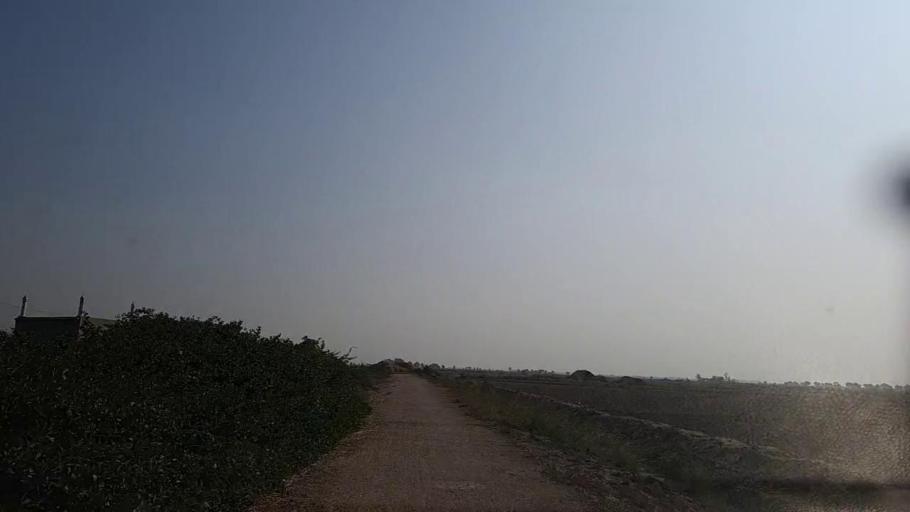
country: PK
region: Sindh
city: Mirpur Batoro
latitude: 24.5788
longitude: 68.2251
